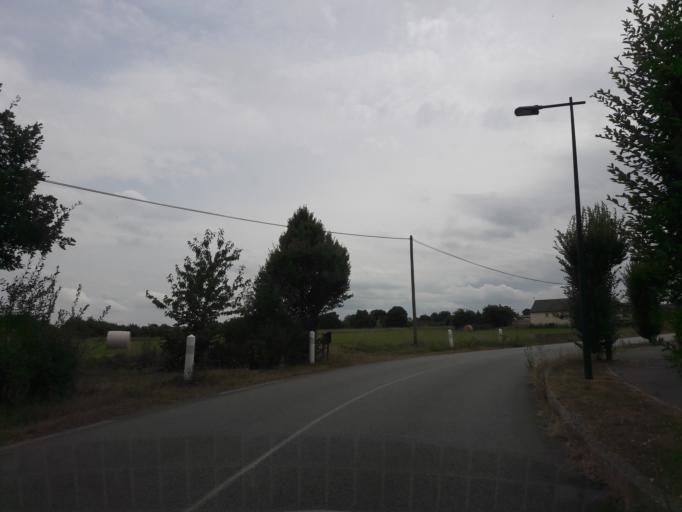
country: FR
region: Brittany
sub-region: Departement d'Ille-et-Vilaine
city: Bain-de-Bretagne
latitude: 47.8497
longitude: -1.6698
